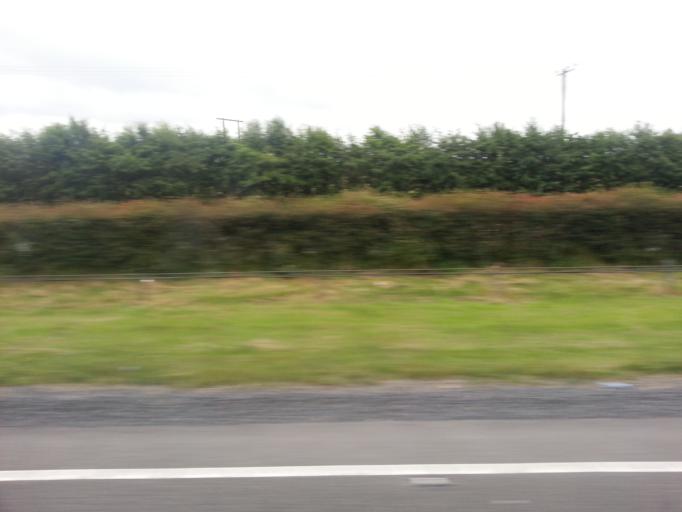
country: IE
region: Leinster
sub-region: Kildare
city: Naas
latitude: 53.2271
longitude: -6.6954
